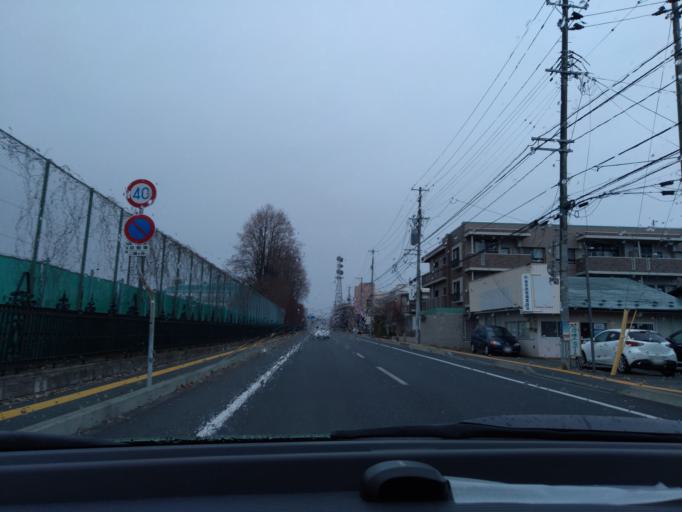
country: JP
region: Iwate
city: Morioka-shi
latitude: 39.7168
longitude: 141.1387
